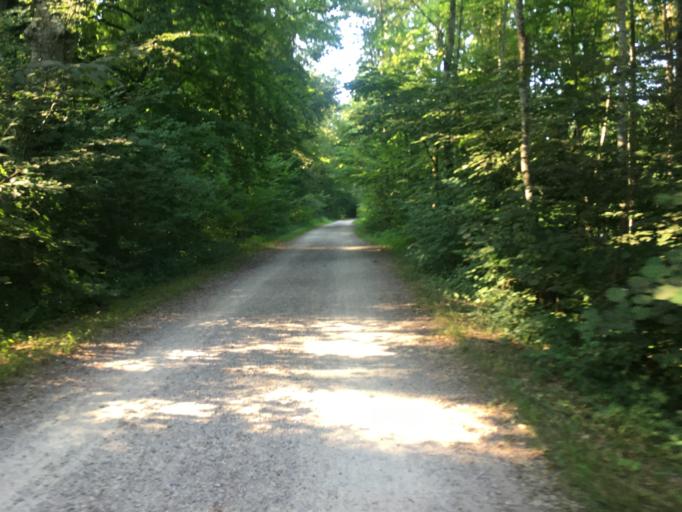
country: CH
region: Bern
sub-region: Emmental District
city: Oberburg
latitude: 47.0427
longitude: 7.6326
